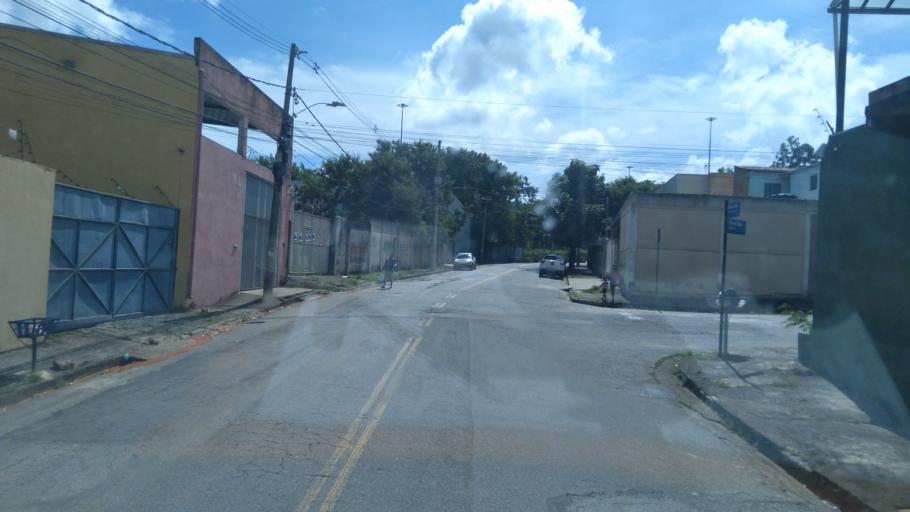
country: BR
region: Minas Gerais
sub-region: Belo Horizonte
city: Belo Horizonte
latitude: -19.8577
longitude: -43.8954
